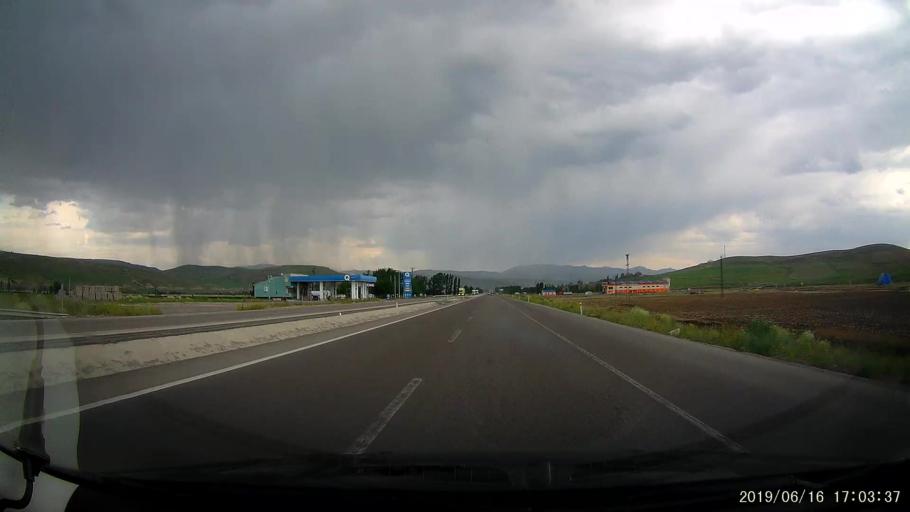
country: TR
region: Erzurum
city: Askale
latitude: 39.9348
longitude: 40.7274
